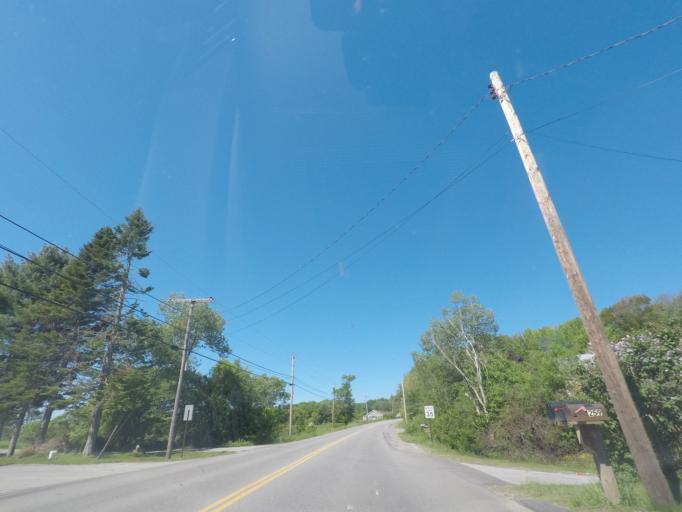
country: US
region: Maine
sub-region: Kennebec County
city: Gardiner
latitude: 44.2315
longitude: -69.7903
